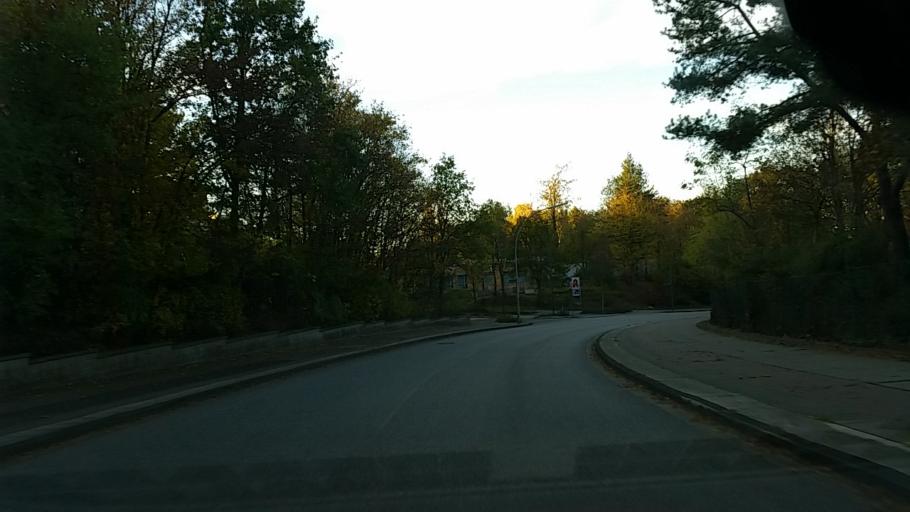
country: DE
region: Schleswig-Holstein
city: Halstenbek
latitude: 53.5745
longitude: 9.8166
